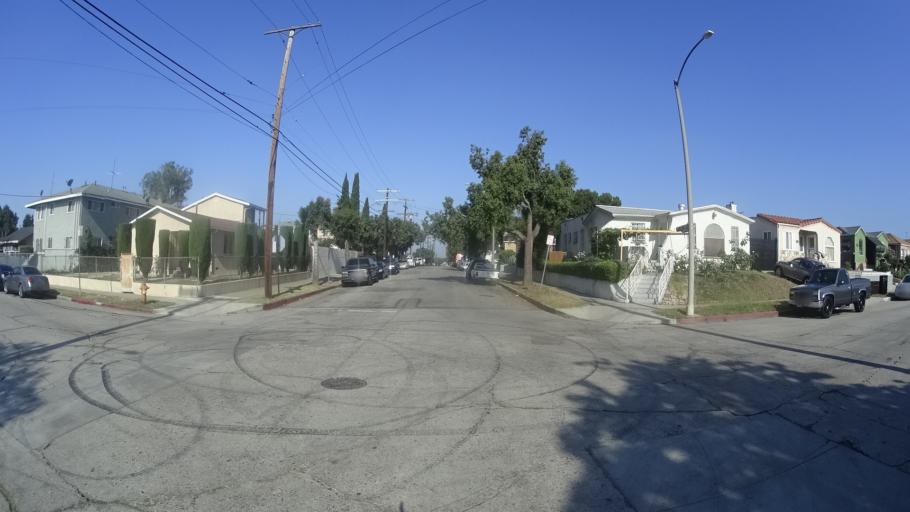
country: US
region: California
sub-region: Los Angeles County
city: View Park-Windsor Hills
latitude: 33.9757
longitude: -118.3279
